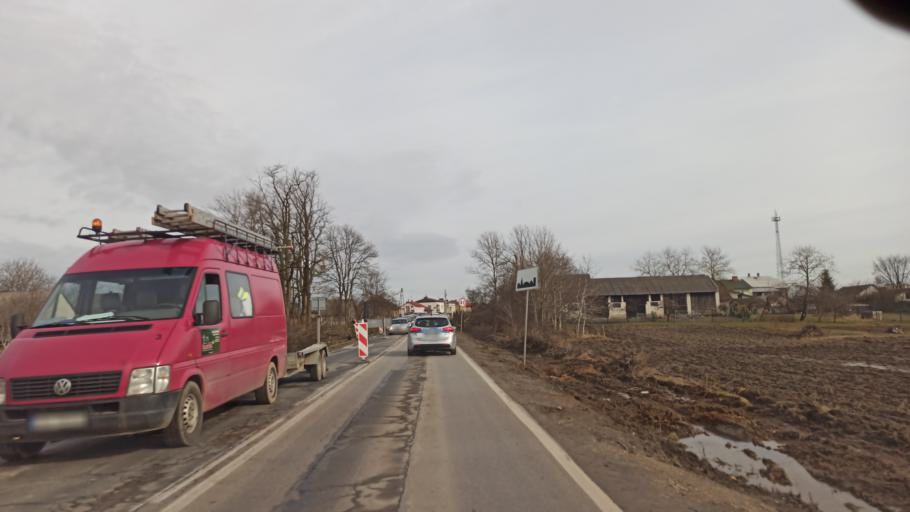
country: PL
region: Lublin Voivodeship
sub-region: Powiat bilgorajski
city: Tarnogrod
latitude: 50.3486
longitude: 22.7346
